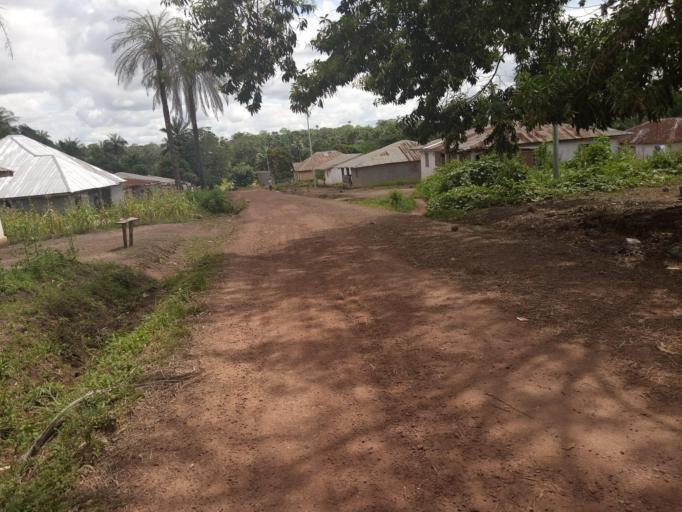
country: SL
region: Northern Province
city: Kamakwie
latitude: 9.4926
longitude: -12.2454
